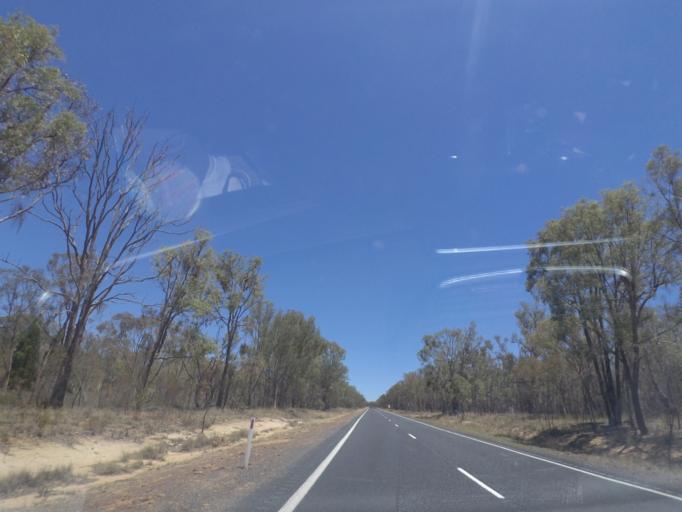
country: AU
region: New South Wales
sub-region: Warrumbungle Shire
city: Coonabarabran
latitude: -31.1689
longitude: 149.3623
